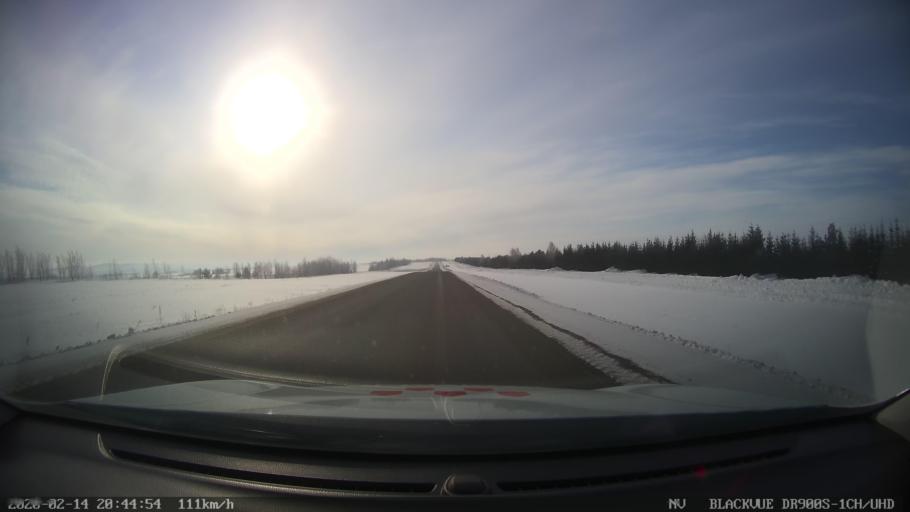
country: RU
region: Tatarstan
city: Kuybyshevskiy Zaton
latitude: 55.2864
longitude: 49.1449
